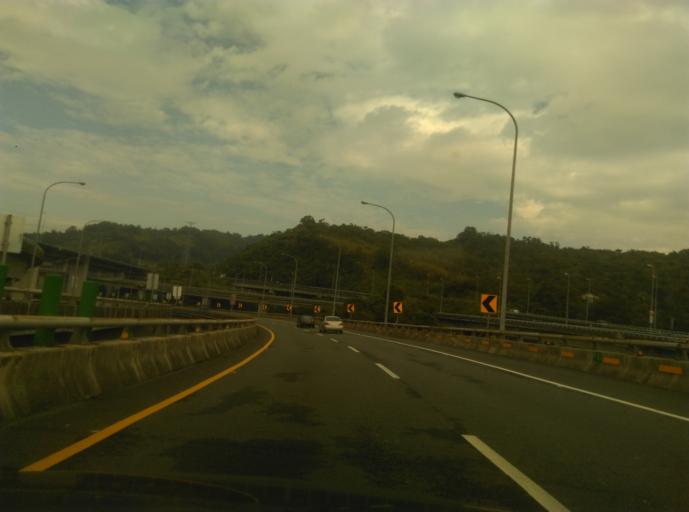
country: TW
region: Taiwan
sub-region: Keelung
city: Keelung
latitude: 25.1240
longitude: 121.6986
